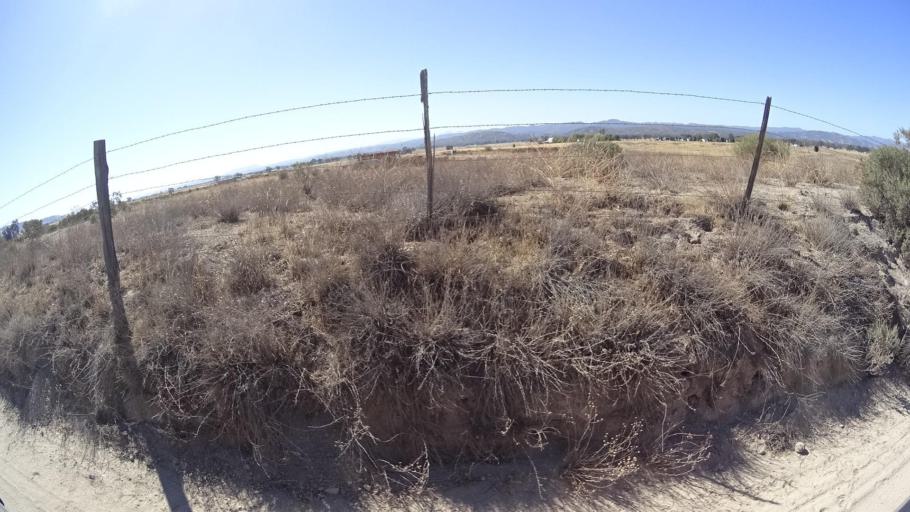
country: US
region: California
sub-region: Monterey County
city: King City
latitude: 35.9516
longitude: -121.0740
